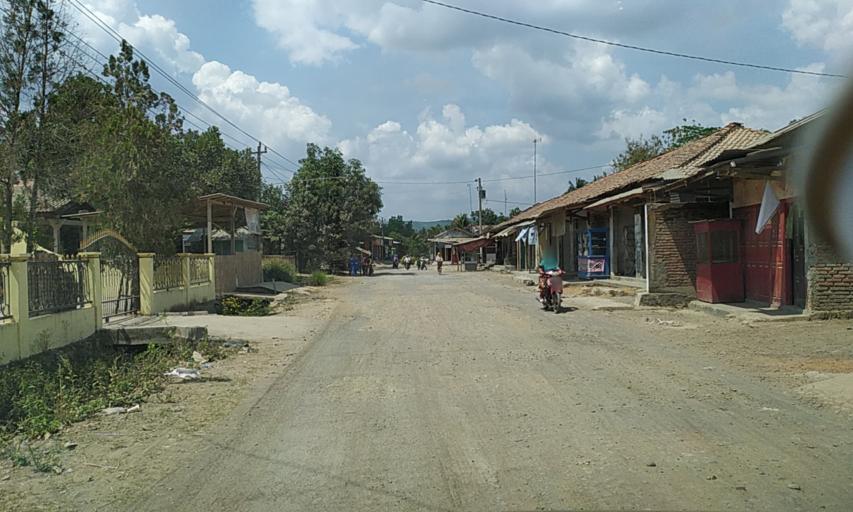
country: ID
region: Central Java
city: Cigintung
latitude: -7.3747
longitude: 108.8029
